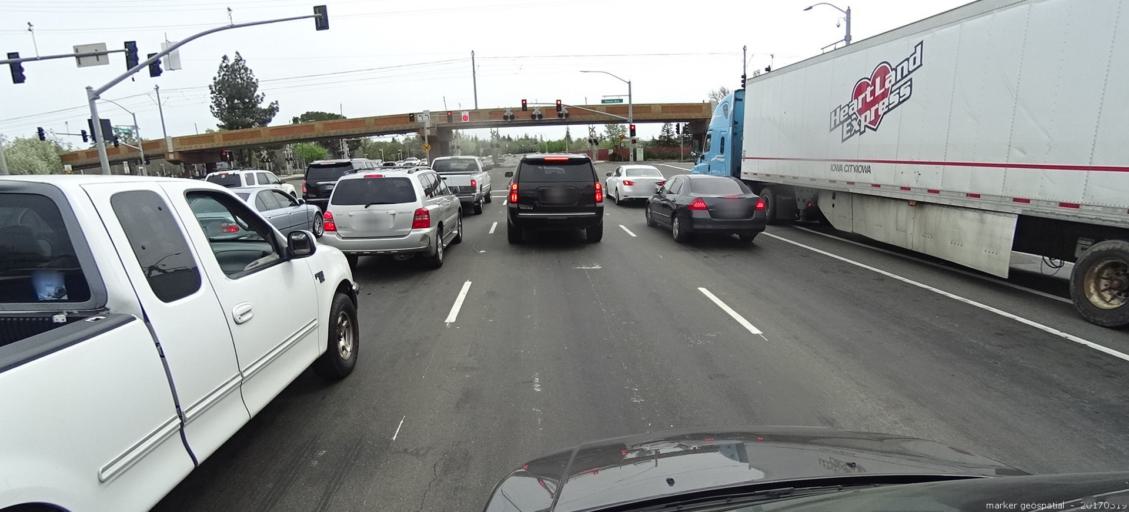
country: US
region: California
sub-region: Sacramento County
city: Rosemont
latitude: 38.5534
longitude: -121.3756
